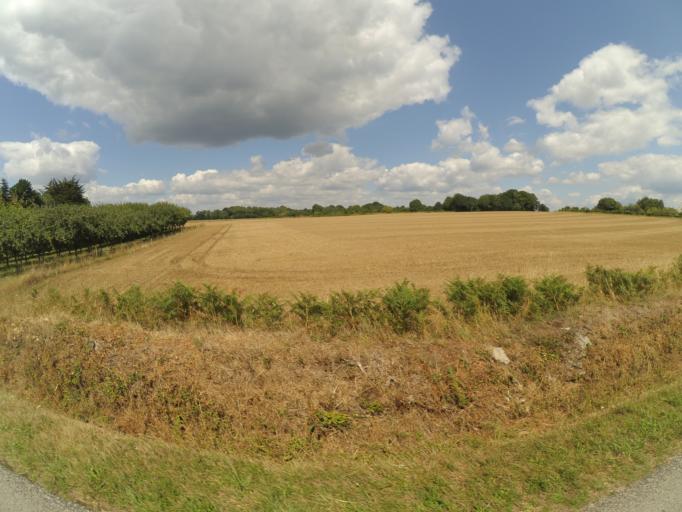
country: FR
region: Brittany
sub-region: Departement du Morbihan
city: Landaul
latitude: 47.7376
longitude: -3.0539
